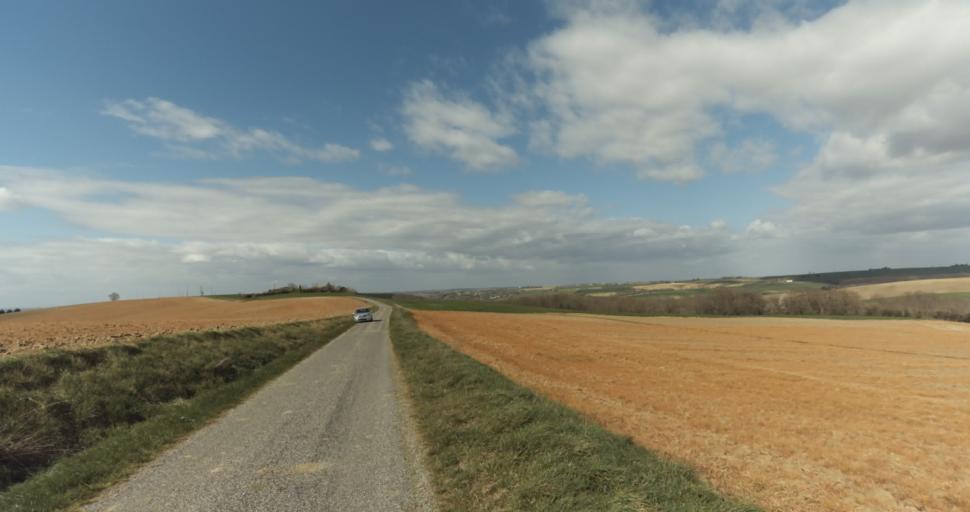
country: FR
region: Midi-Pyrenees
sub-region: Departement de la Haute-Garonne
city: Auterive
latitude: 43.3597
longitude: 1.5149
